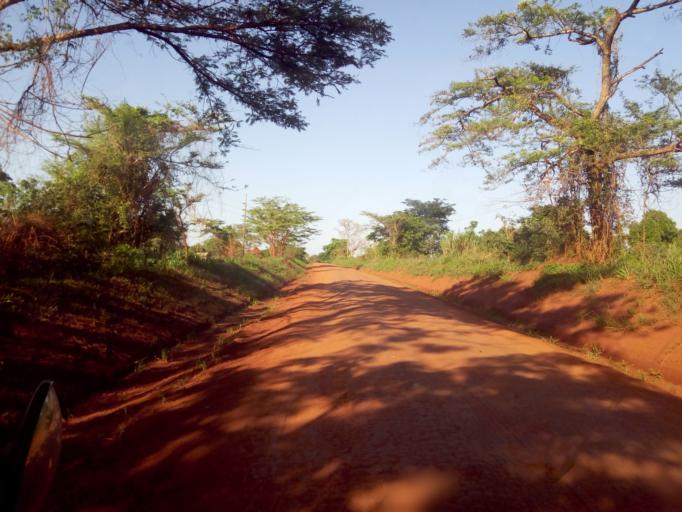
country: UG
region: Western Region
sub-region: Masindi District
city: Masindi
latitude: 1.7761
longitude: 31.8454
